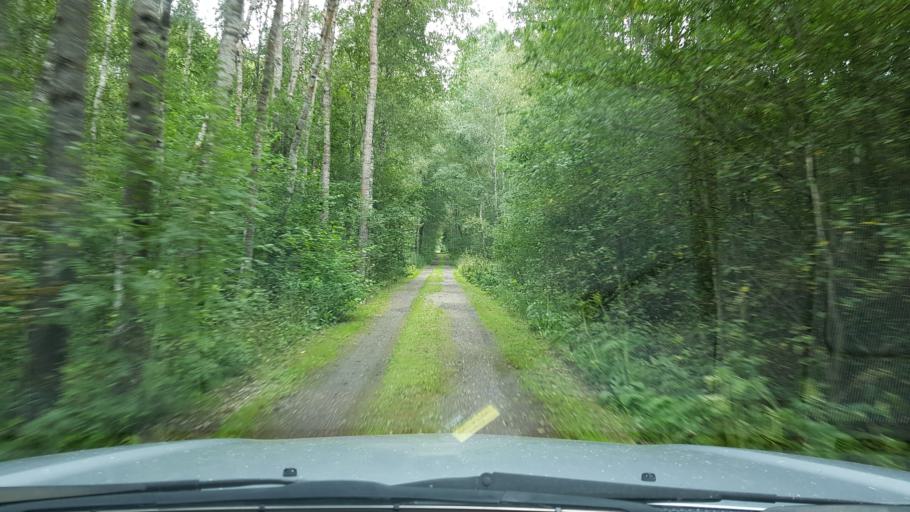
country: EE
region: Harju
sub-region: Joelaehtme vald
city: Loo
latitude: 59.3879
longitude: 24.9736
